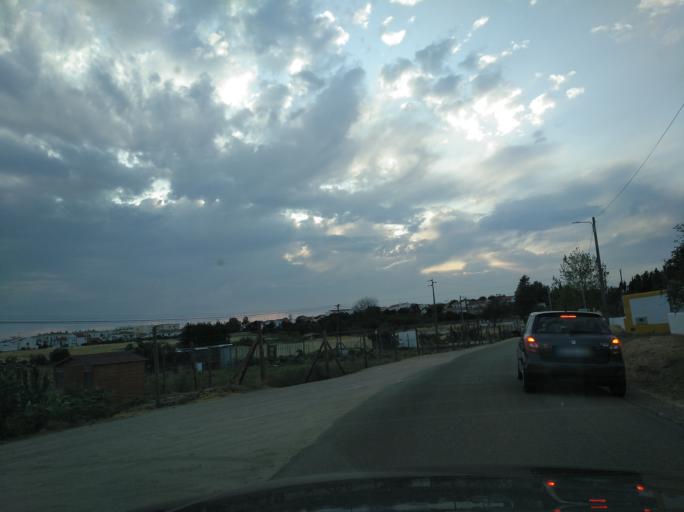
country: PT
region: Portalegre
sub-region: Campo Maior
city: Campo Maior
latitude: 39.0177
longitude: -7.0554
